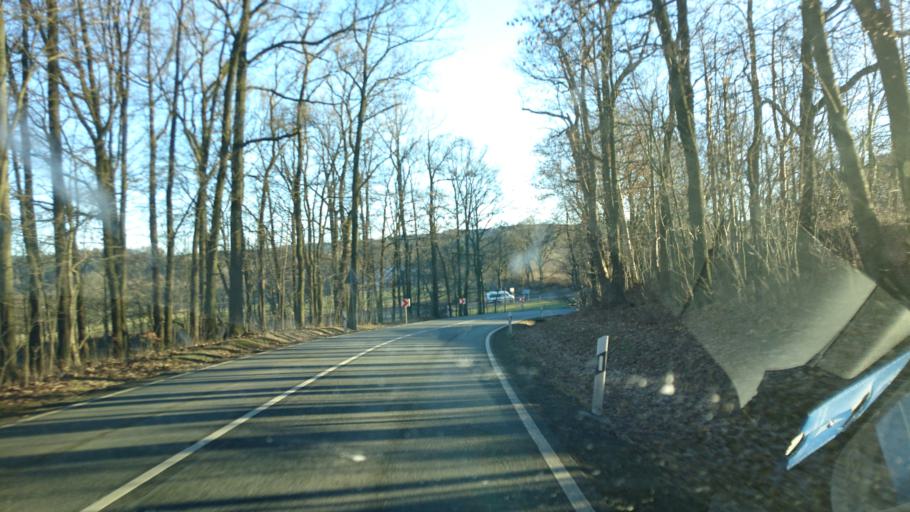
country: DE
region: Thuringia
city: Lohma
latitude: 50.5799
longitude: 11.8451
